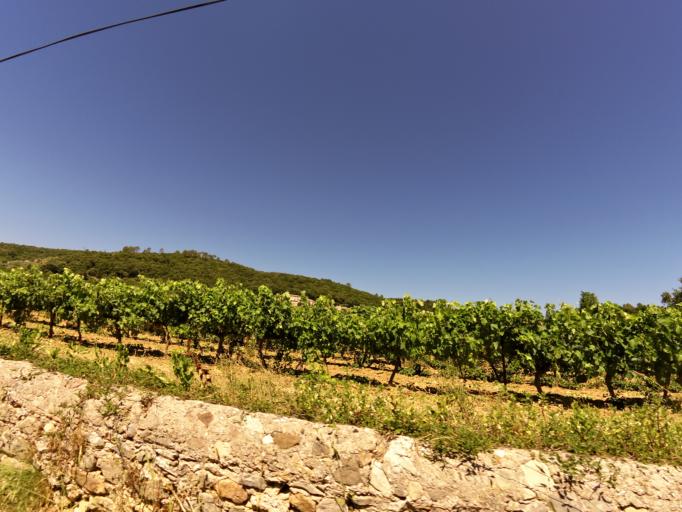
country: FR
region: Languedoc-Roussillon
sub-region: Departement du Gard
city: Boisset-et-Gaujac
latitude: 44.0220
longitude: 3.9911
